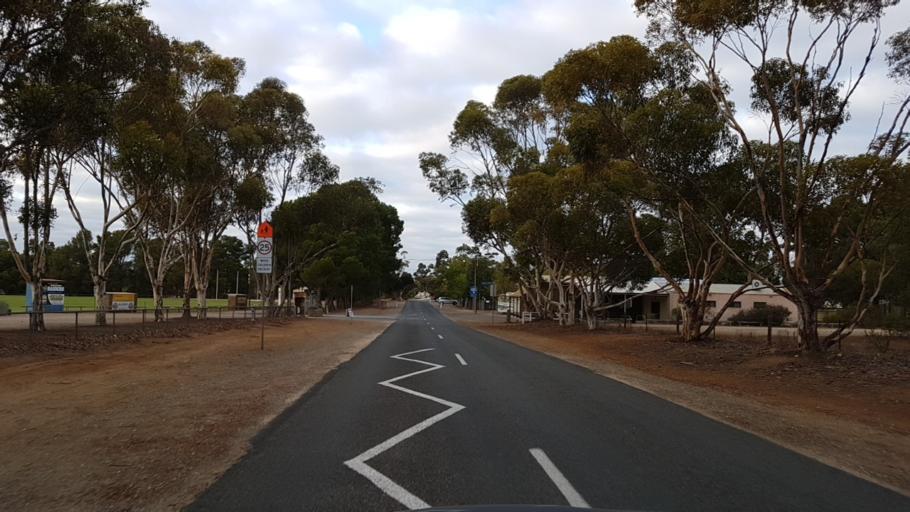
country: AU
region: South Australia
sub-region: Mount Barker
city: Callington
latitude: -35.1128
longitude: 139.0391
